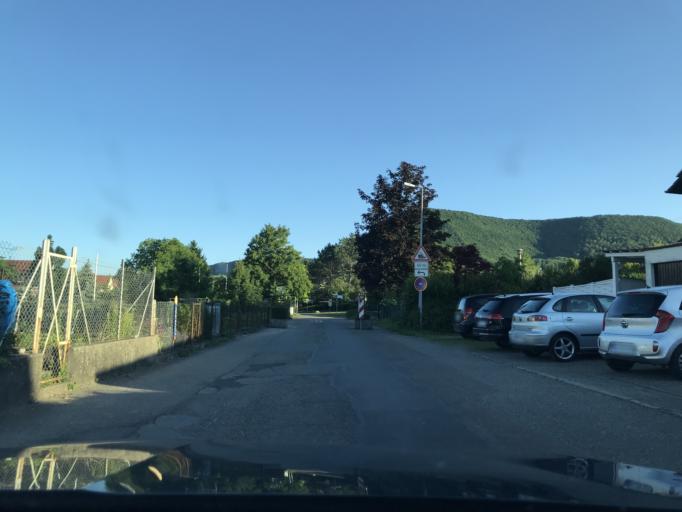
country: DE
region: Baden-Wuerttemberg
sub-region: Regierungsbezirk Stuttgart
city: Owen
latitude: 48.5854
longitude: 9.4475
